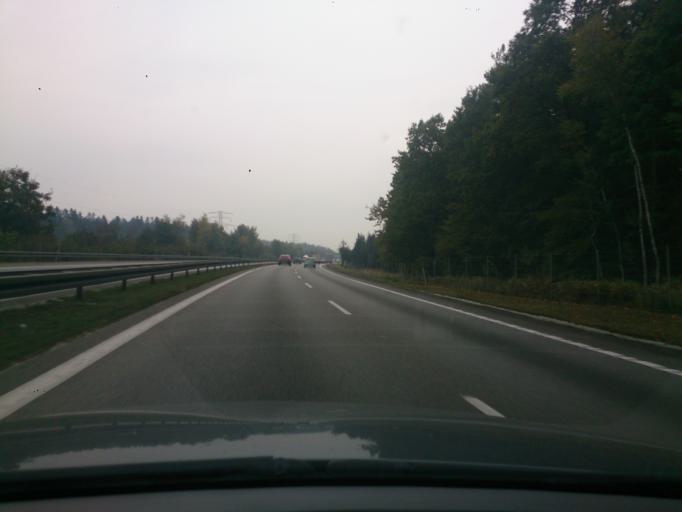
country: PL
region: Pomeranian Voivodeship
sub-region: Gdynia
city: Wielki Kack
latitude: 54.3995
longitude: 18.4853
